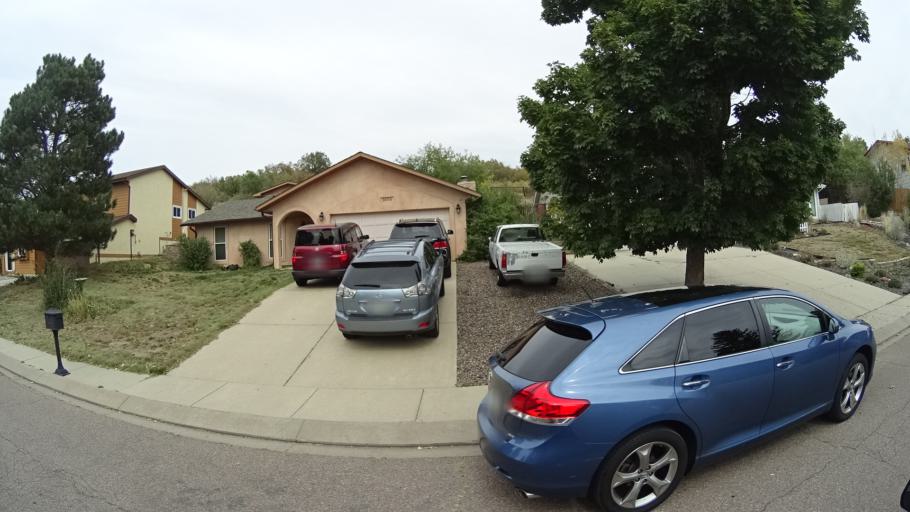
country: US
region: Colorado
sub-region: El Paso County
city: Cimarron Hills
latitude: 38.9048
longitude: -104.7233
